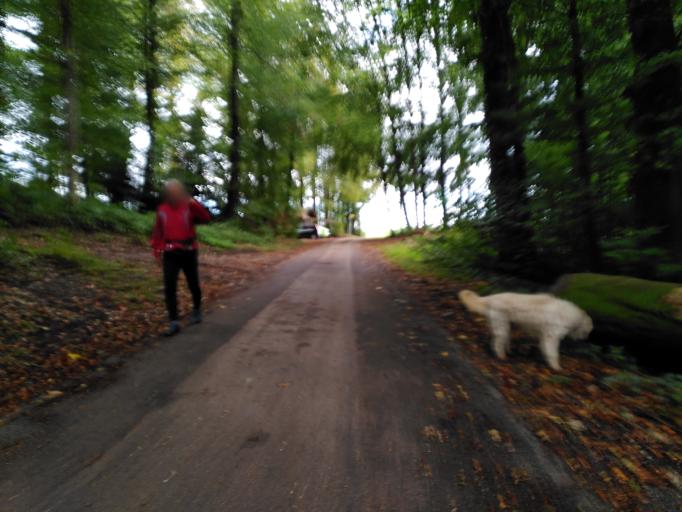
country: CH
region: Bern
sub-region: Emmental District
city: Ersigen
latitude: 47.0973
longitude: 7.6086
